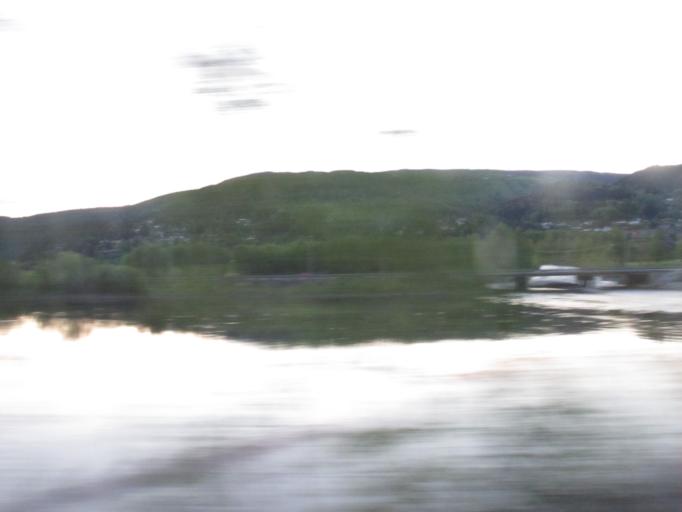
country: NO
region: Oppland
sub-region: Ringebu
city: Ringebu
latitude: 61.4523
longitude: 10.1827
